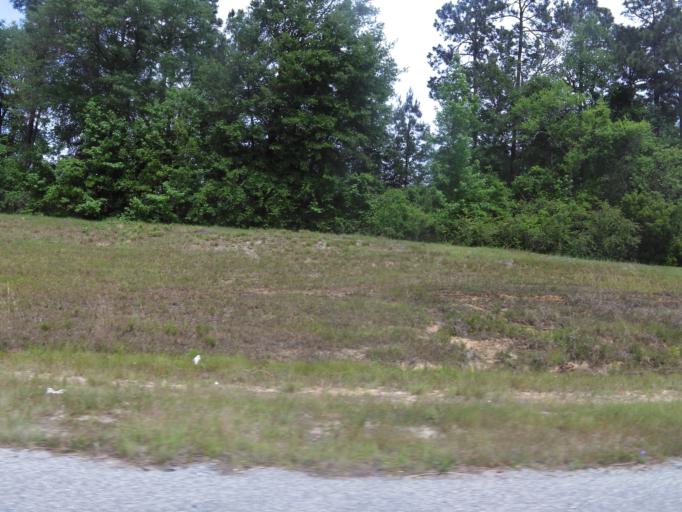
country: US
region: Georgia
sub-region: Emanuel County
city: Swainsboro
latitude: 32.5905
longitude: -82.3691
